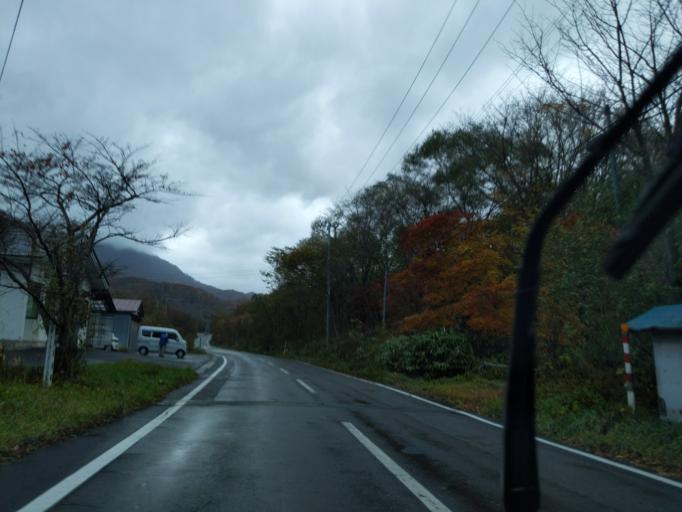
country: JP
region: Iwate
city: Ichinoseki
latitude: 39.0141
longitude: 140.8843
